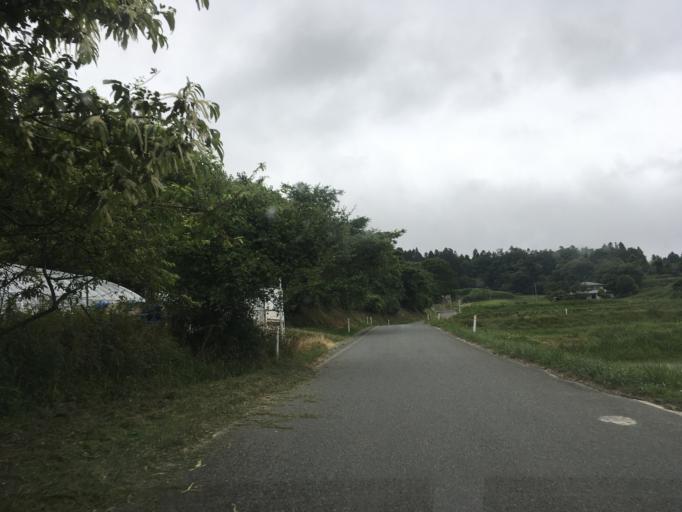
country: JP
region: Iwate
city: Ichinoseki
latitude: 38.8799
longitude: 141.3732
